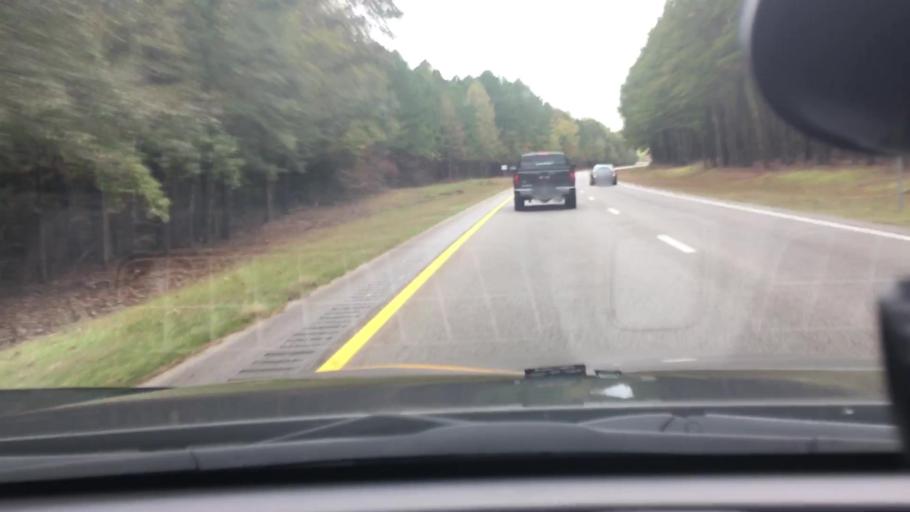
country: US
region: North Carolina
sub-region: Wake County
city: Zebulon
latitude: 35.7950
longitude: -78.1619
